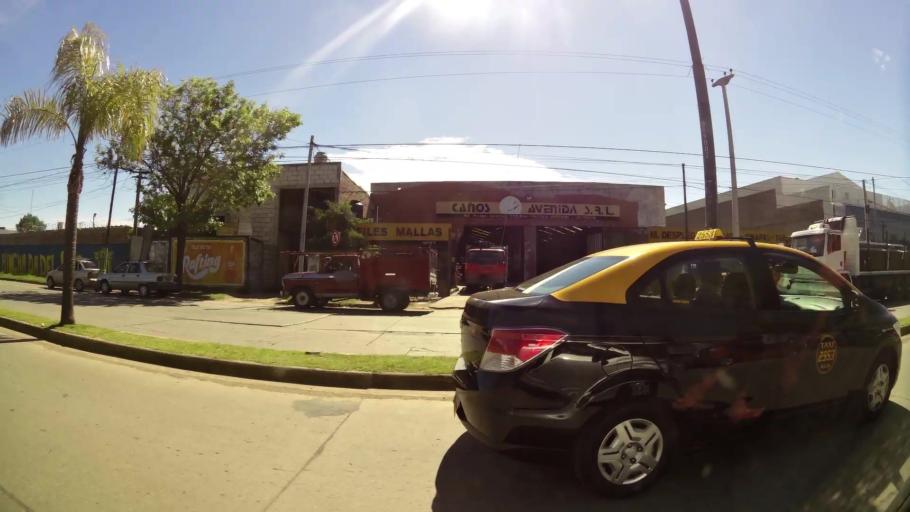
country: AR
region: Santa Fe
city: Granadero Baigorria
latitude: -32.9281
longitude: -60.7132
